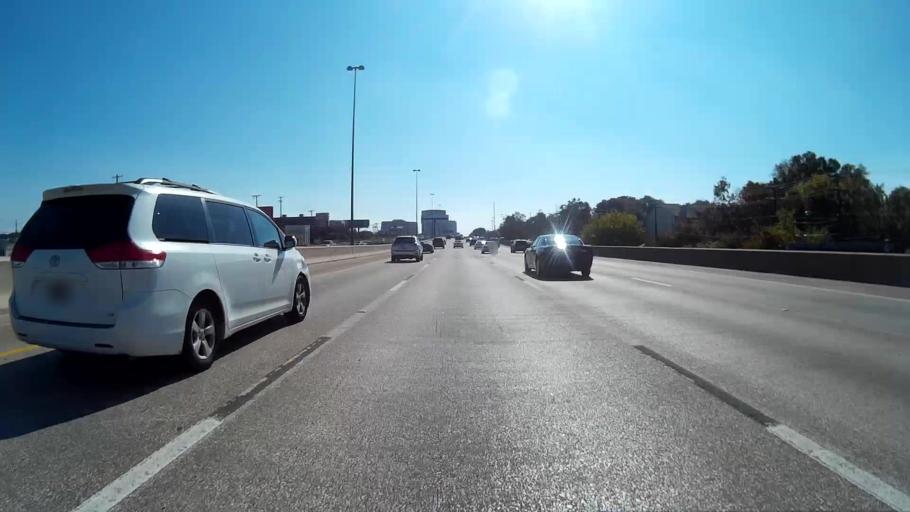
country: US
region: Texas
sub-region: Dallas County
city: University Park
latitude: 32.8988
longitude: -96.7692
